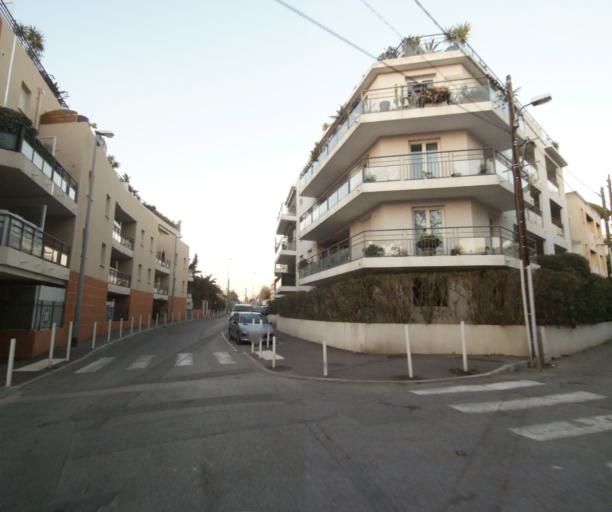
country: FR
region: Provence-Alpes-Cote d'Azur
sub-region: Departement des Alpes-Maritimes
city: Antibes
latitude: 43.5716
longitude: 7.1136
